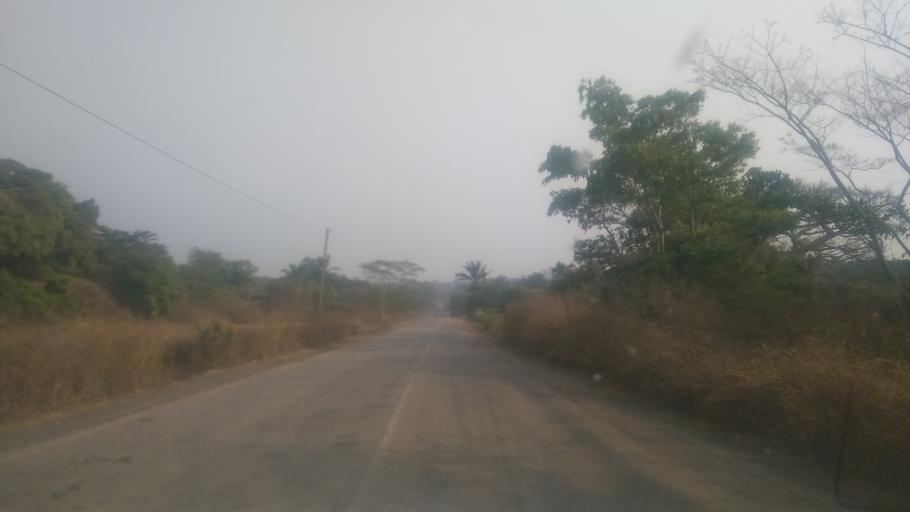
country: CM
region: West
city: Tonga
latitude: 4.9996
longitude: 10.6992
